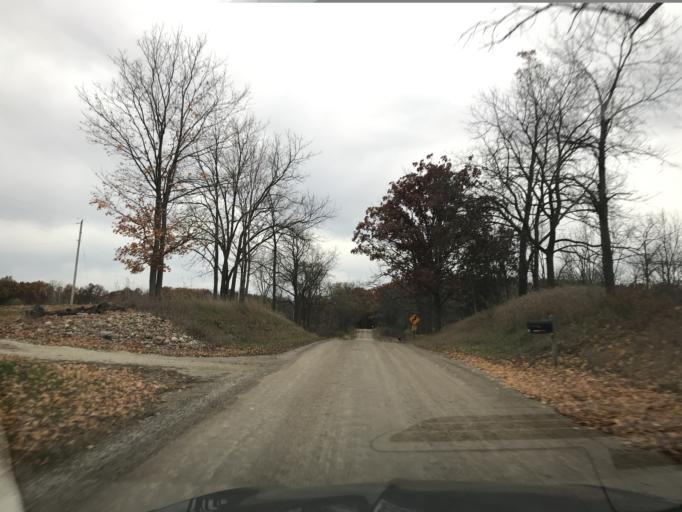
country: US
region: Michigan
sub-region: Lenawee County
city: Manitou Beach-Devils Lake
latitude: 42.0229
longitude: -84.3351
